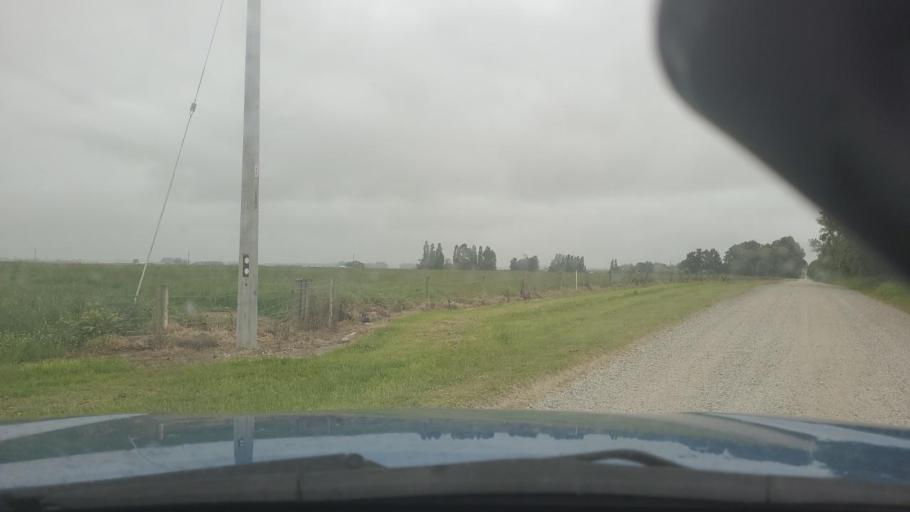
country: NZ
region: Southland
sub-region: Gore District
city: Gore
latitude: -46.3299
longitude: 168.7910
